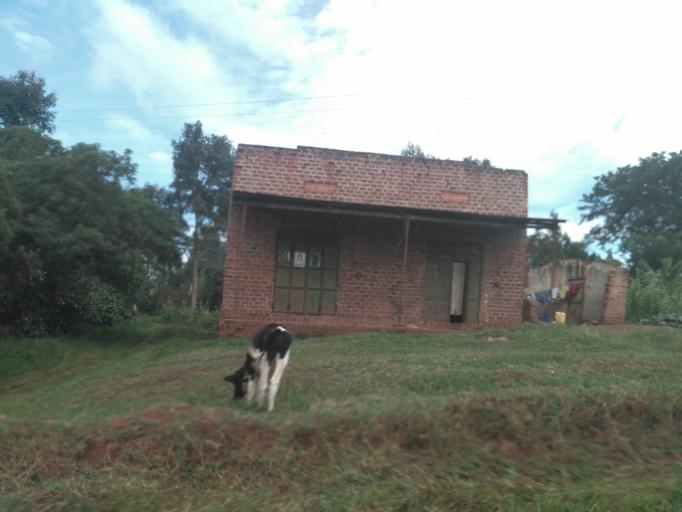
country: UG
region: Central Region
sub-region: Buikwe District
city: Njeru
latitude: 0.4074
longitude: 33.1795
